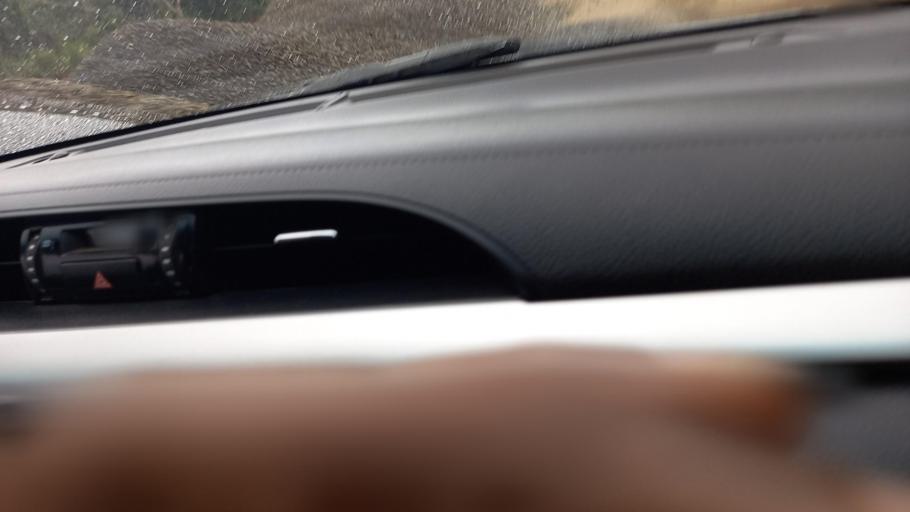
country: ET
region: Southern Nations, Nationalities, and People's Region
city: Mizan Teferi
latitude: 6.1873
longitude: 35.6885
